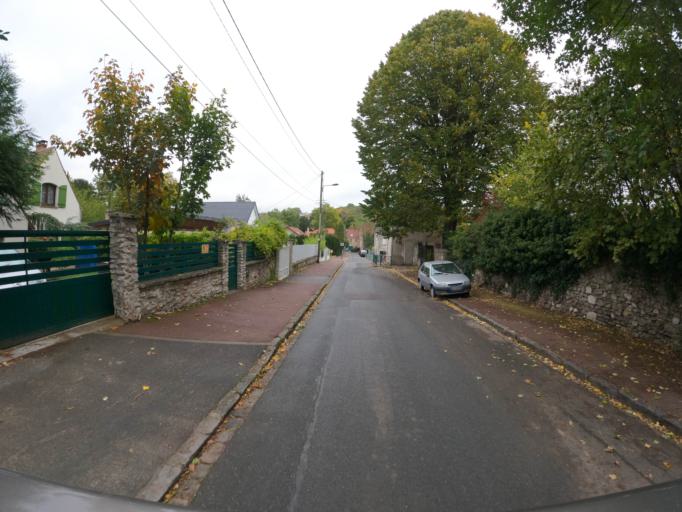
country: FR
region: Ile-de-France
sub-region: Departement du Val-de-Marne
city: Sucy-en-Brie
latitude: 48.7753
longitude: 2.5189
